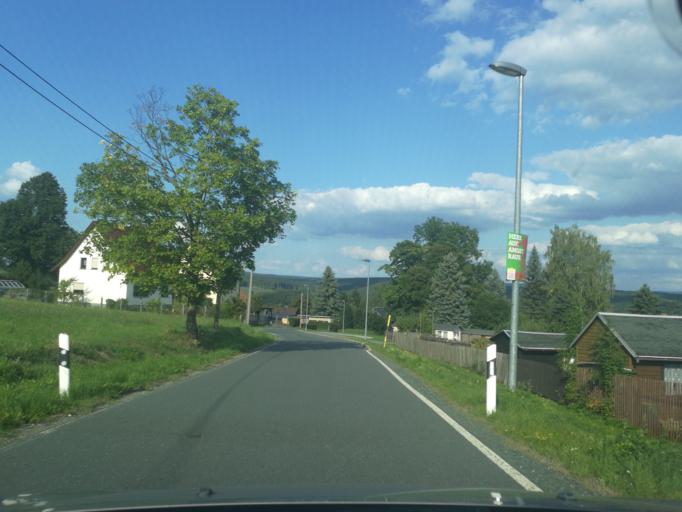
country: DE
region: Saxony
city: Adorf
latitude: 50.3192
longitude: 12.2460
